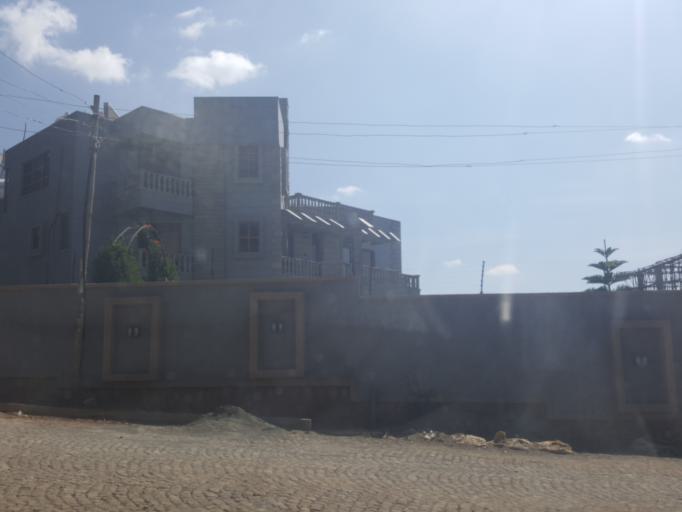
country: ET
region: Adis Abeba
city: Addis Ababa
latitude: 9.0703
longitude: 38.7173
